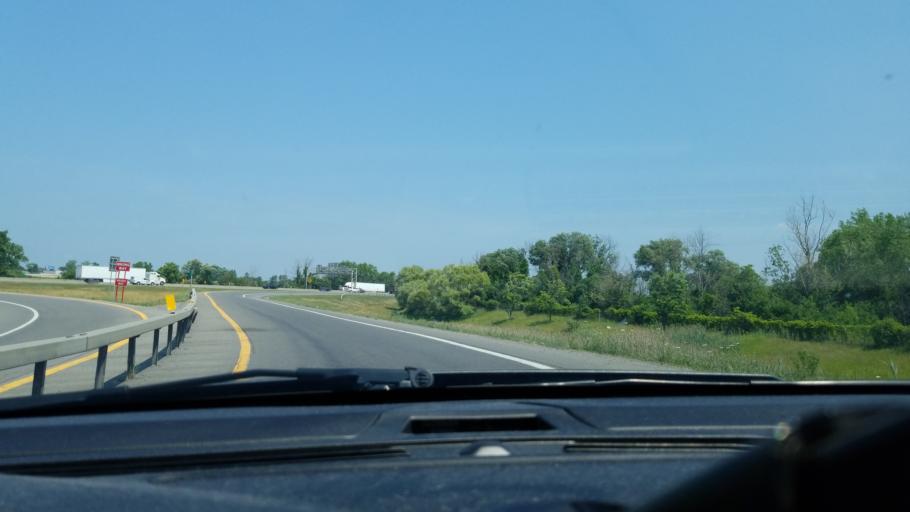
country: US
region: New York
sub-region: Onondaga County
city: Galeville
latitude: 43.0897
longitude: -76.1644
